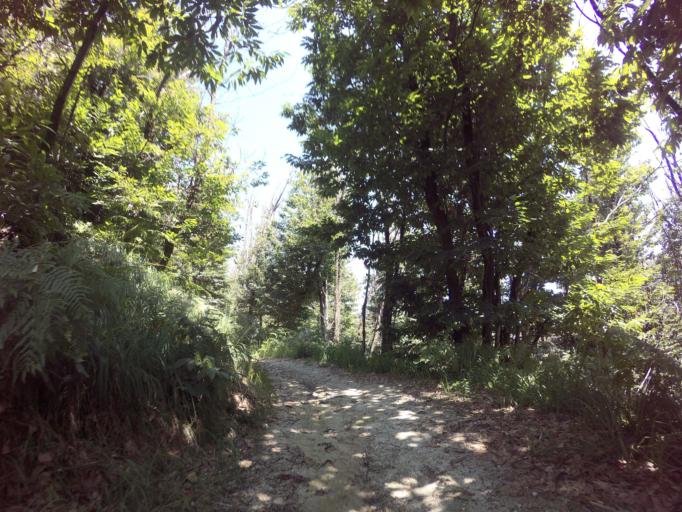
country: IT
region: Piedmont
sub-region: Provincia di Cuneo
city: Chiusa di Pesio
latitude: 44.2946
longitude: 7.6914
